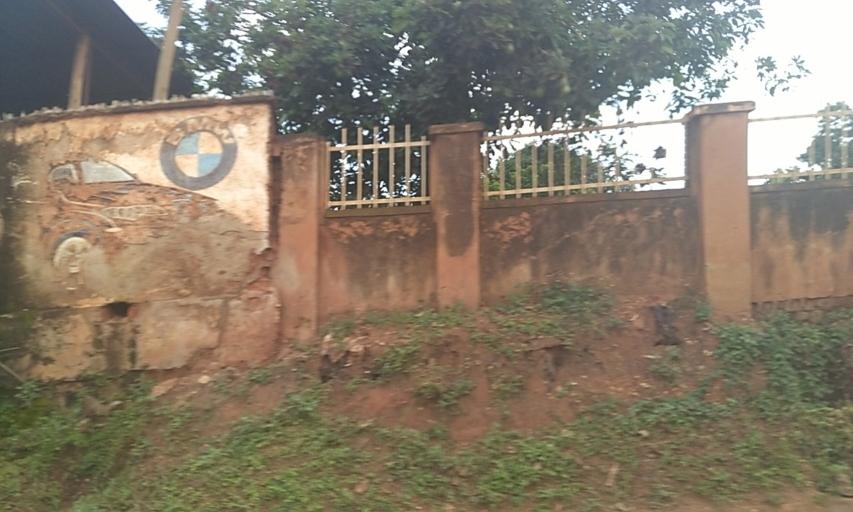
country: UG
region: Central Region
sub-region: Wakiso District
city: Kireka
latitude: 0.3427
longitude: 32.6254
